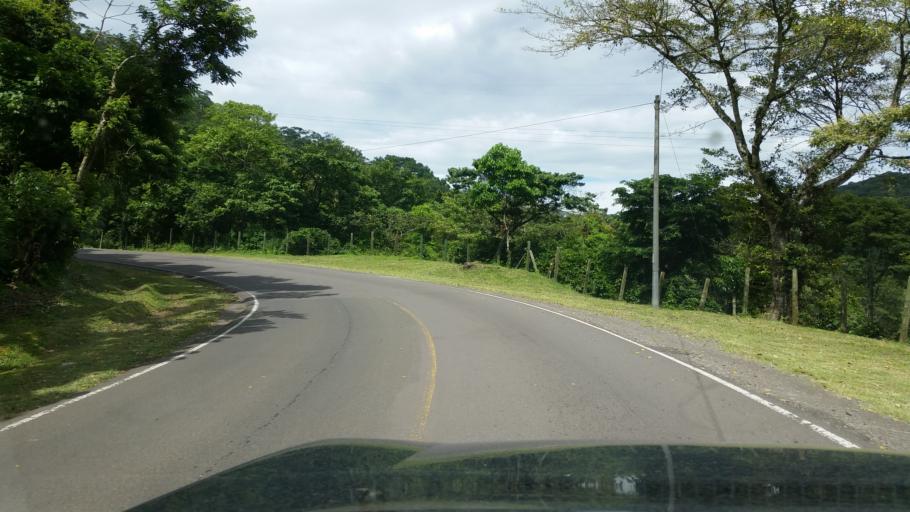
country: NI
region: Matagalpa
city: San Ramon
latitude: 12.9595
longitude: -85.8624
